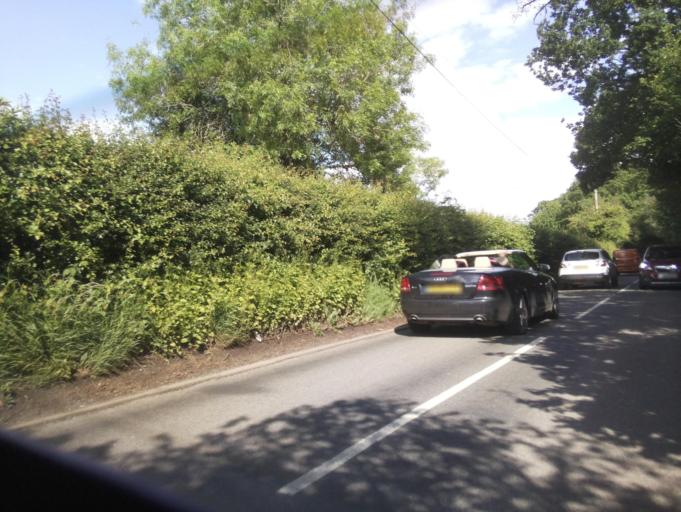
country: GB
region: England
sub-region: Hertfordshire
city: Chorleywood
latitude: 51.6590
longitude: -0.4598
